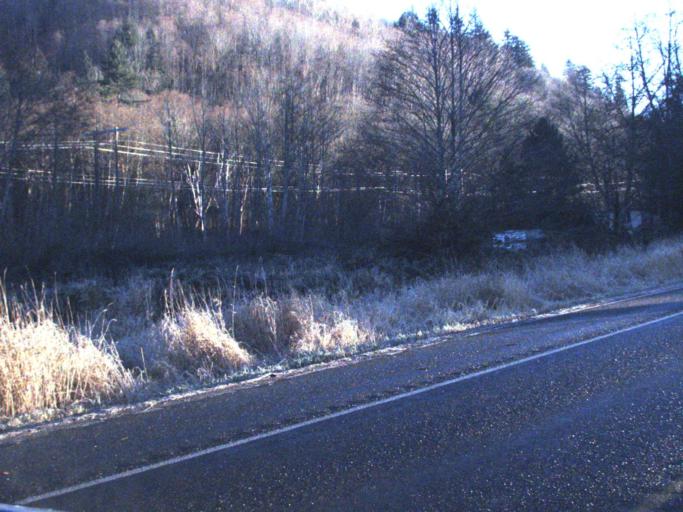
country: US
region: Washington
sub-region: Skagit County
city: Sedro-Woolley
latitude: 48.5299
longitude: -122.0793
